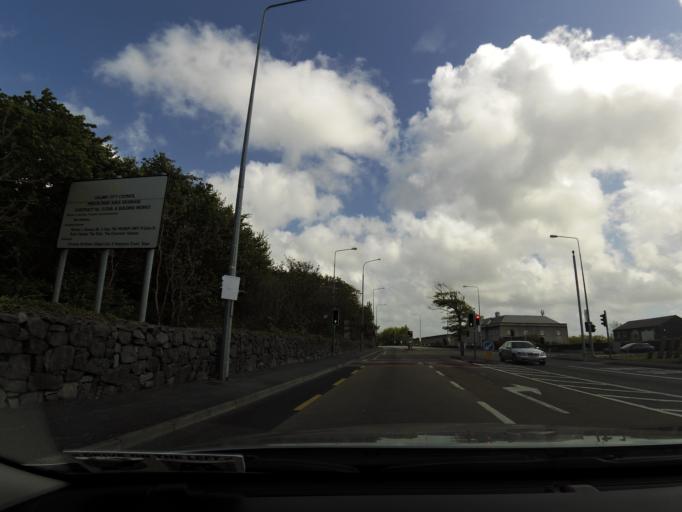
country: IE
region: Connaught
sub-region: County Galway
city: Gaillimh
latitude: 53.2750
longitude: -8.9994
